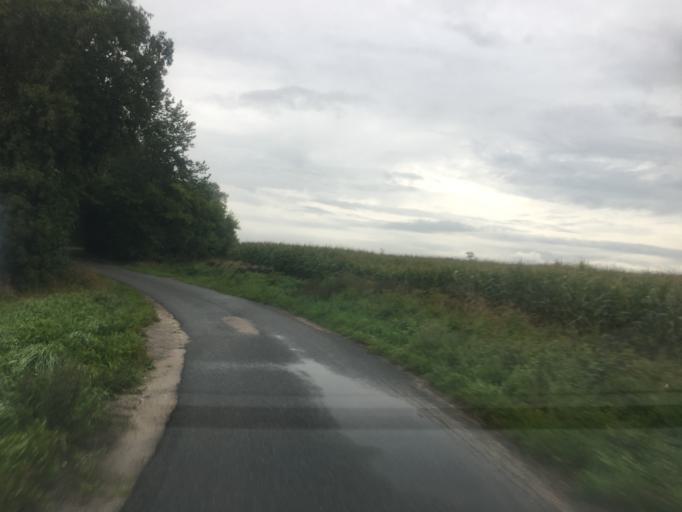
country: DK
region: South Denmark
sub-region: Tonder Kommune
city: Logumkloster
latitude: 54.9791
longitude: 8.9636
